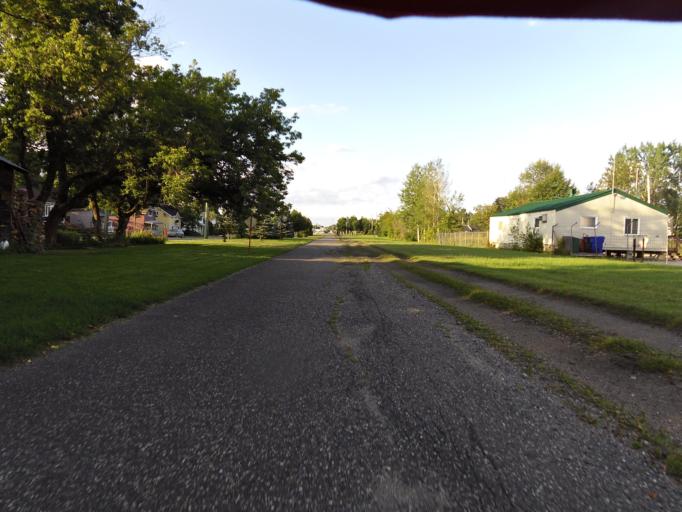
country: CA
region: Quebec
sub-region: Outaouais
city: Maniwaki
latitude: 46.3714
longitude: -75.9781
